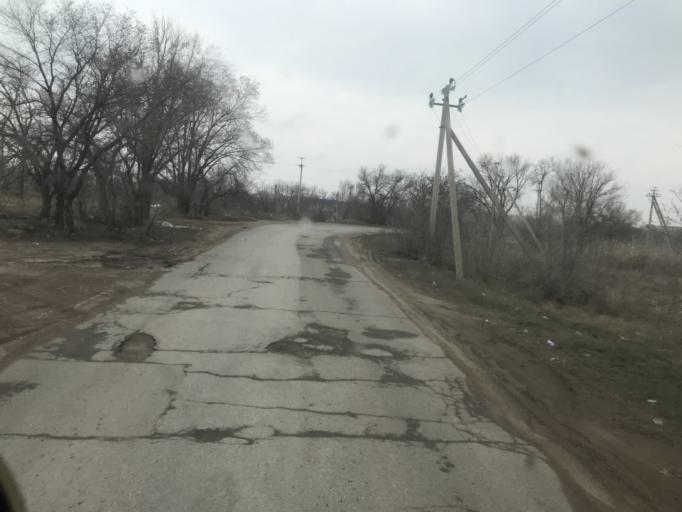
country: RU
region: Volgograd
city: Krasnoslobodsk
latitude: 48.5336
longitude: 44.6063
